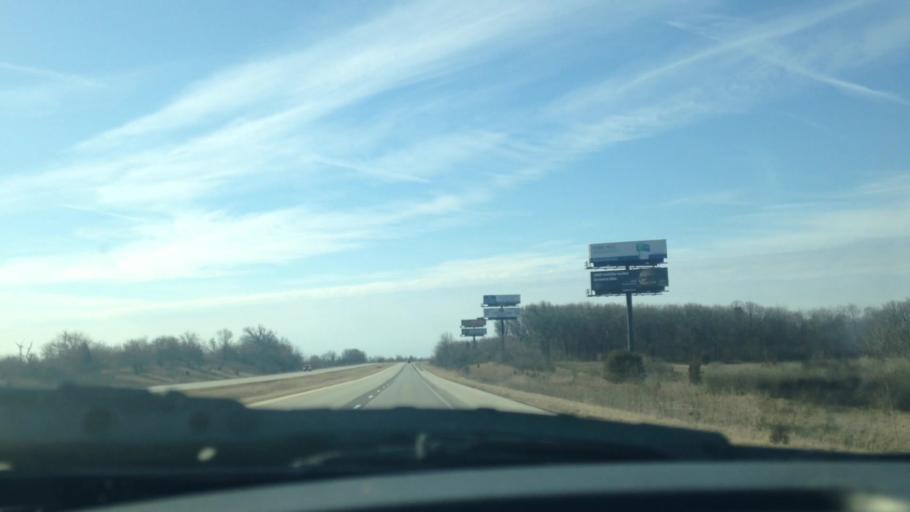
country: US
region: Illinois
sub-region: Ford County
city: Paxton
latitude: 40.5167
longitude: -88.0848
